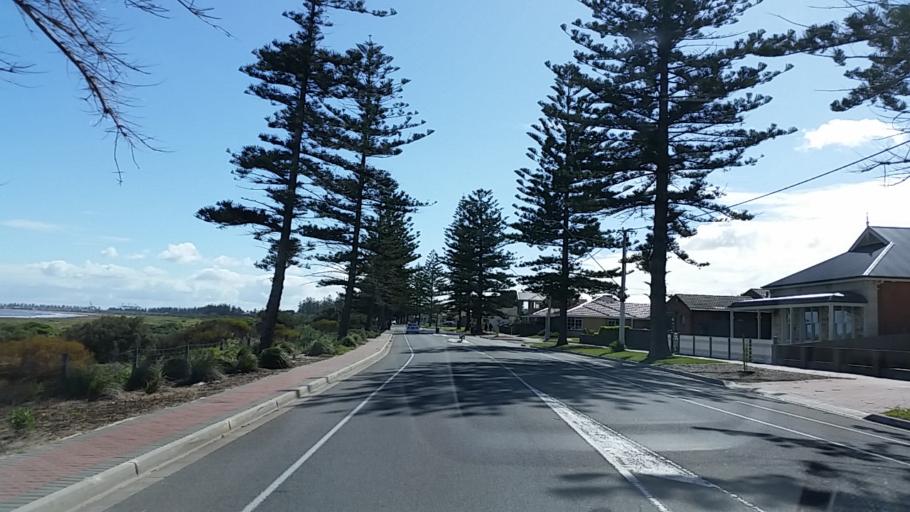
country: AU
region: South Australia
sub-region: Port Adelaide Enfield
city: Birkenhead
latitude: -34.8219
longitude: 138.4885
